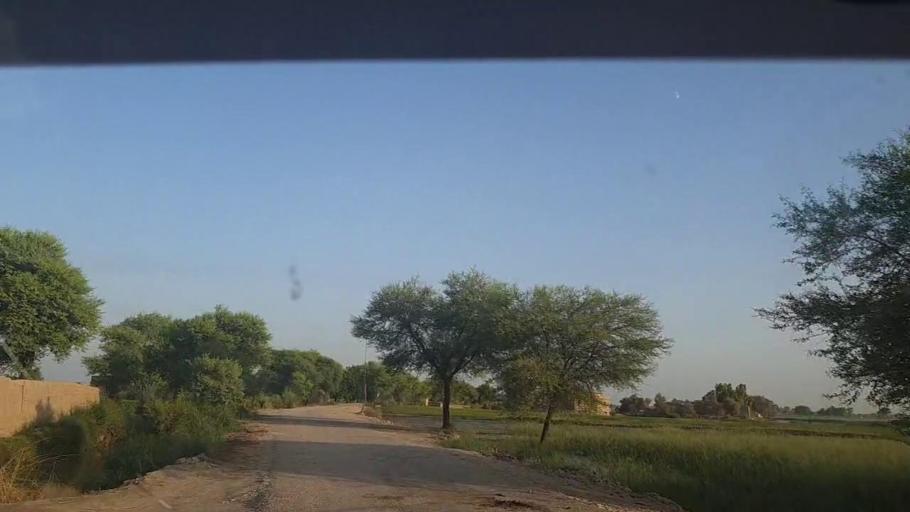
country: PK
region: Sindh
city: Thul
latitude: 28.1206
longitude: 68.8954
